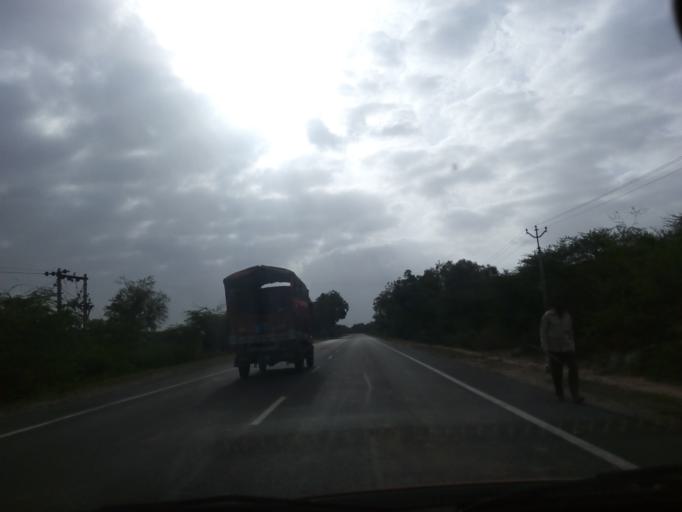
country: IN
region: Gujarat
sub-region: Kachchh
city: Bhachau
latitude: 23.3336
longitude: 70.1842
